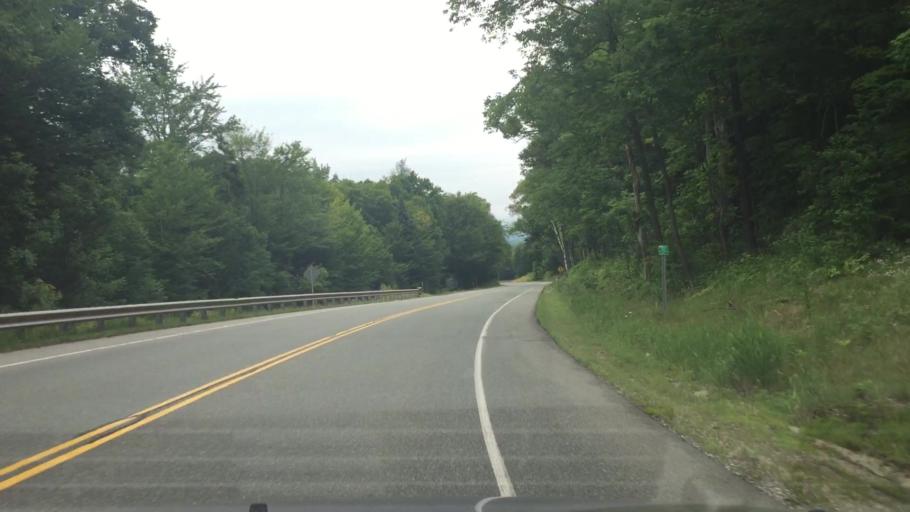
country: US
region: New Hampshire
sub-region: Grafton County
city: Deerfield
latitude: 44.2443
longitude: -71.6500
